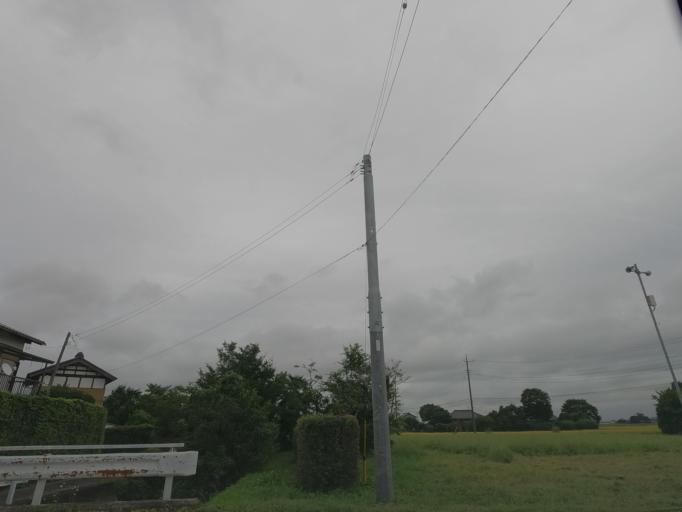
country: JP
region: Ibaraki
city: Toride
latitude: 35.9238
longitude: 140.0723
